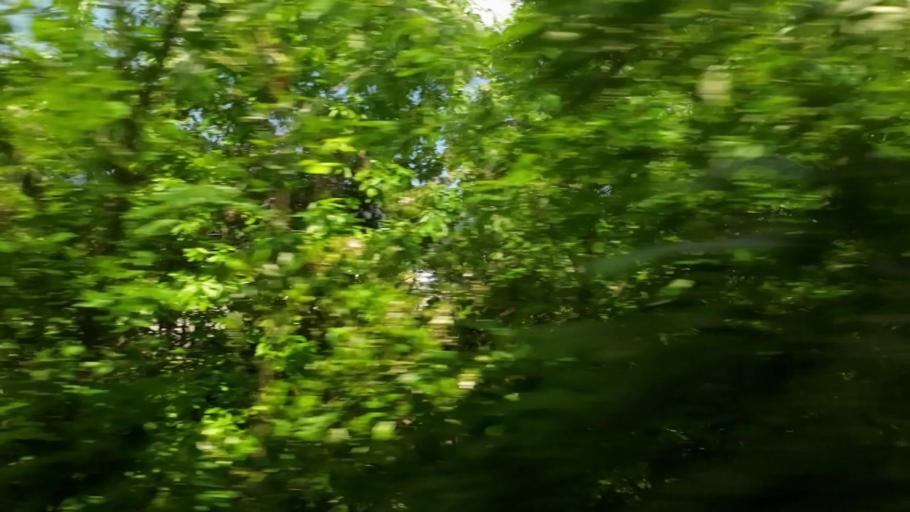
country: JP
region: Kagawa
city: Kan'onjicho
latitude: 34.1699
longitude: 133.6912
